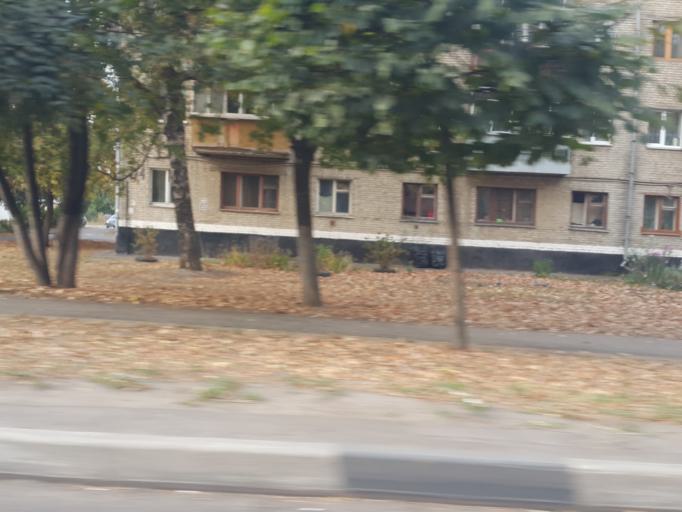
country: RU
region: Tambov
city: Bokino
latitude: 52.6805
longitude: 41.4635
